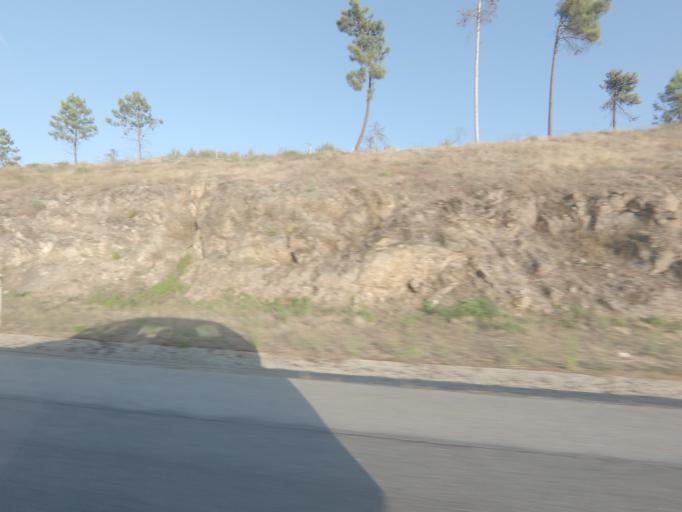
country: PT
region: Vila Real
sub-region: Vila Real
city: Vila Real
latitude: 41.3055
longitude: -7.6880
